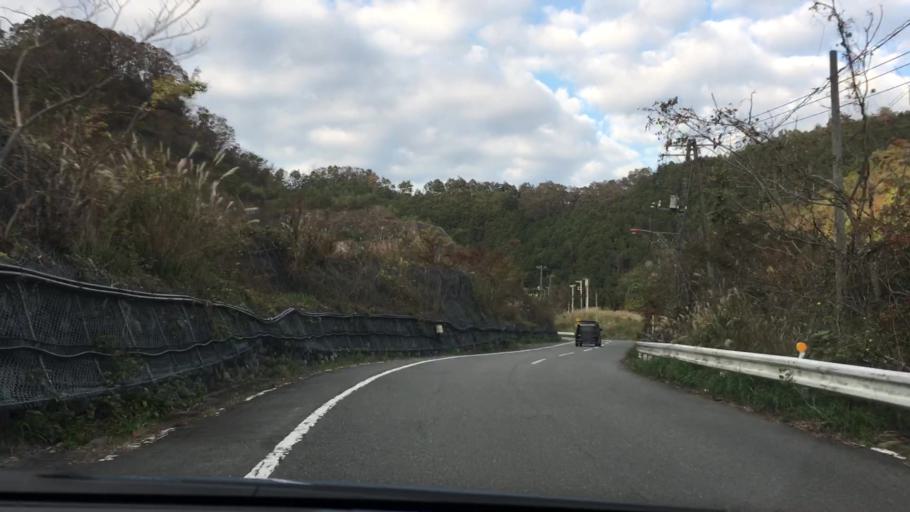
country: JP
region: Yamanashi
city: Uenohara
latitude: 35.5558
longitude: 139.1387
